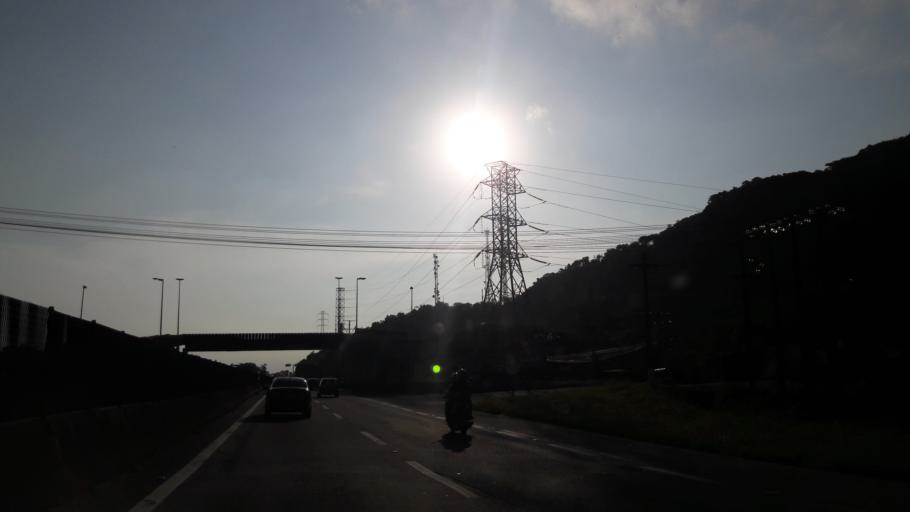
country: BR
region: Sao Paulo
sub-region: Mongagua
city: Mongagua
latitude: -24.0968
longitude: -46.6282
